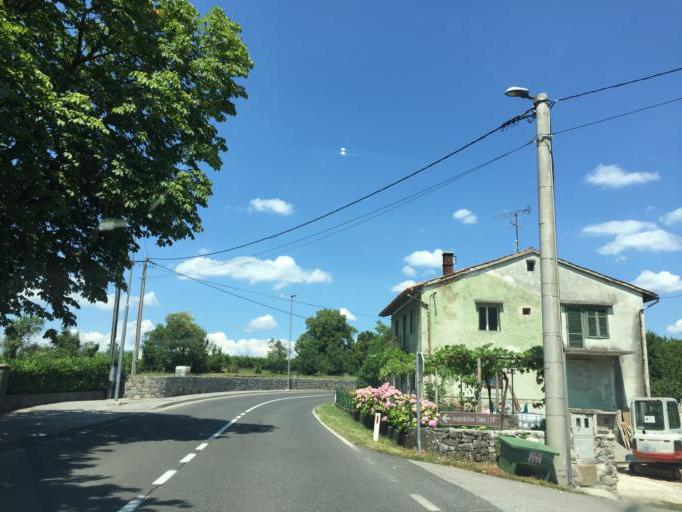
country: SI
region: Sezana
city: Sezana
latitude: 45.7220
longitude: 13.8671
